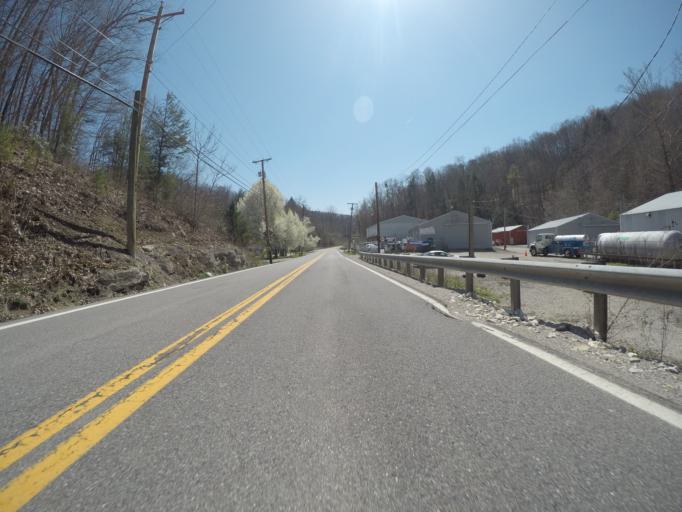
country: US
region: West Virginia
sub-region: Kanawha County
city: Pinch
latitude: 38.3883
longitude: -81.5595
